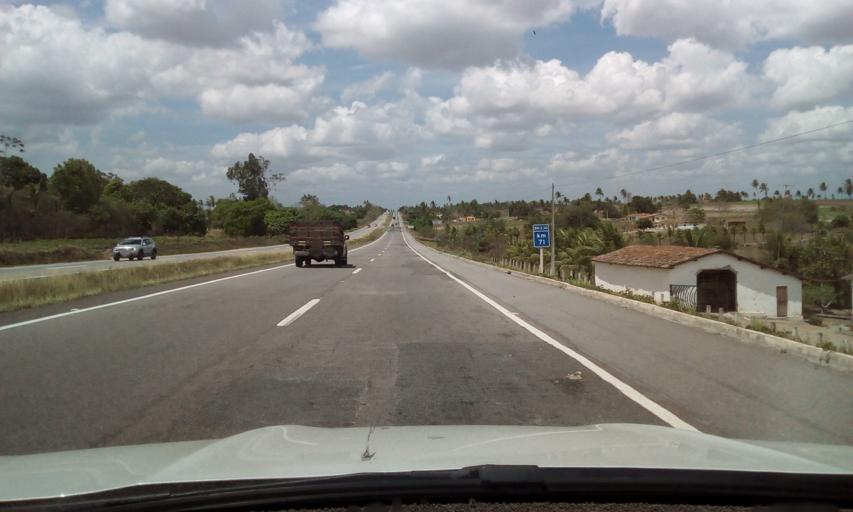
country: BR
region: Paraiba
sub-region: Pilar
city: Pilar
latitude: -7.1907
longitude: -35.2417
